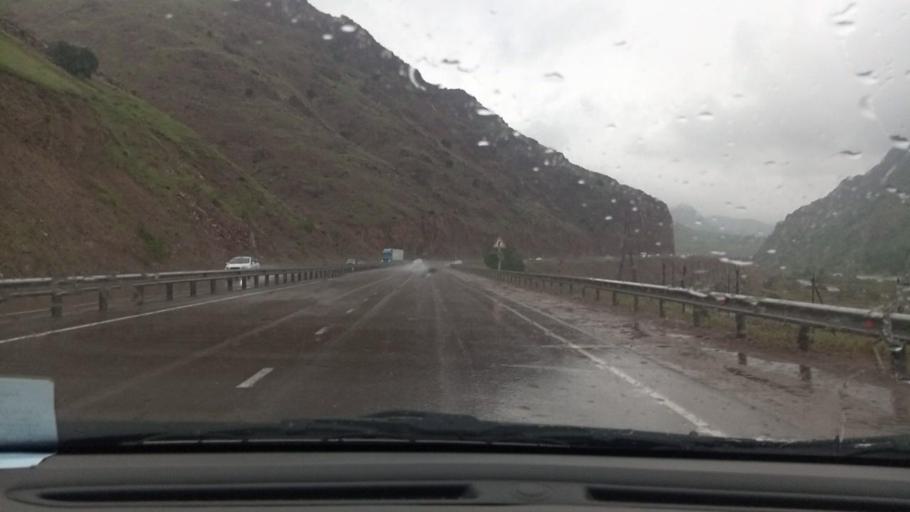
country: UZ
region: Toshkent
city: Angren
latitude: 41.1137
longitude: 70.3395
